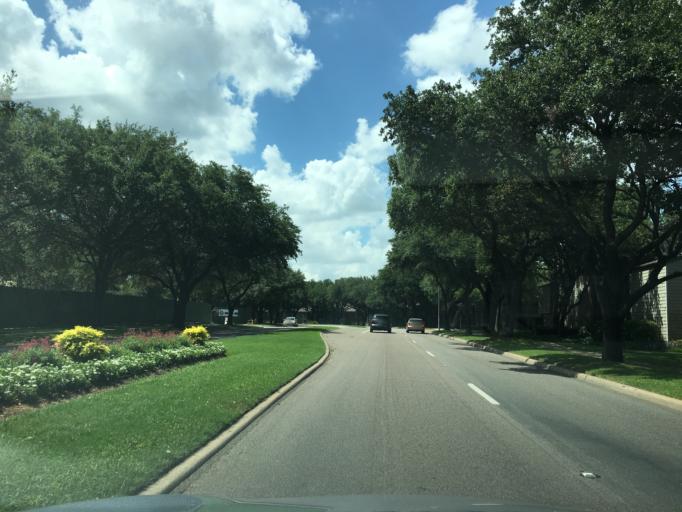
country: US
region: Texas
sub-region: Dallas County
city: University Park
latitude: 32.8598
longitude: -96.7609
